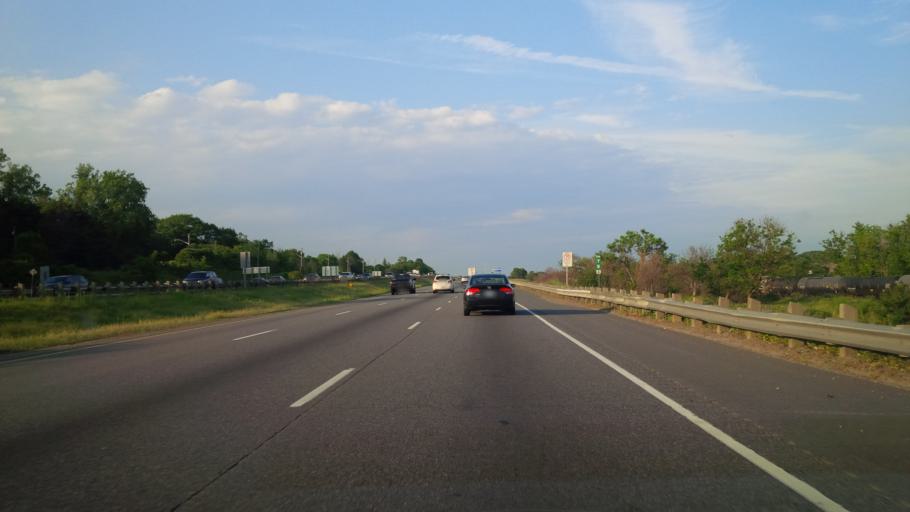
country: CA
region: Ontario
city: Hamilton
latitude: 43.3003
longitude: -79.8768
